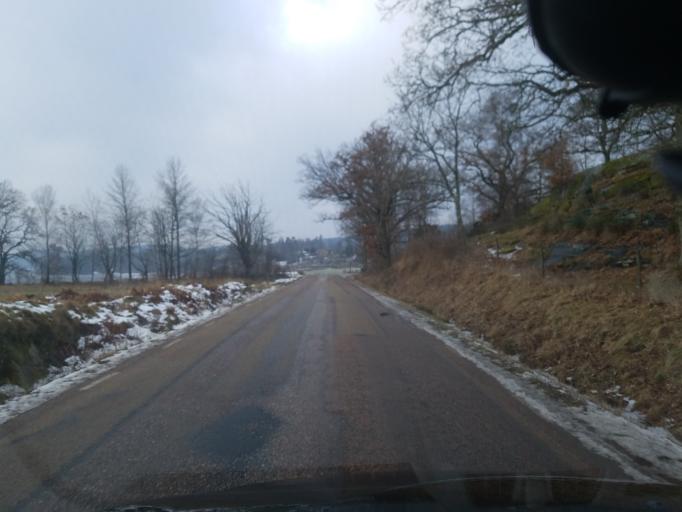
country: SE
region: Vaestra Goetaland
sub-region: Orust
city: Henan
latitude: 58.3128
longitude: 11.6809
